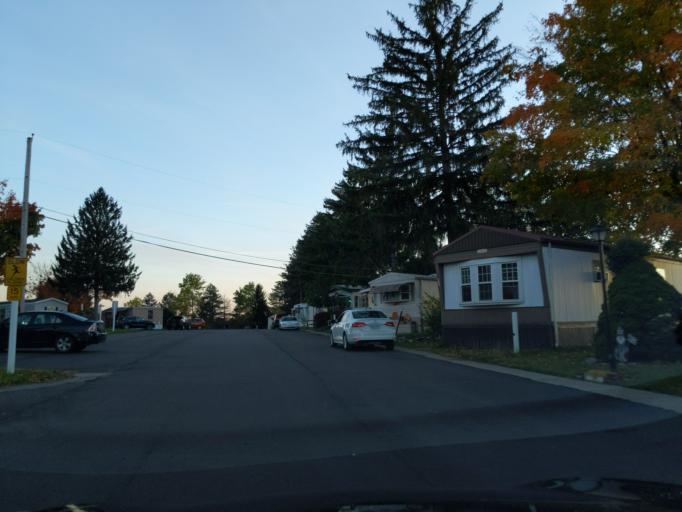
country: US
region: Michigan
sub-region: Ingham County
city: Edgemont Park
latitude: 42.7245
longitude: -84.5996
